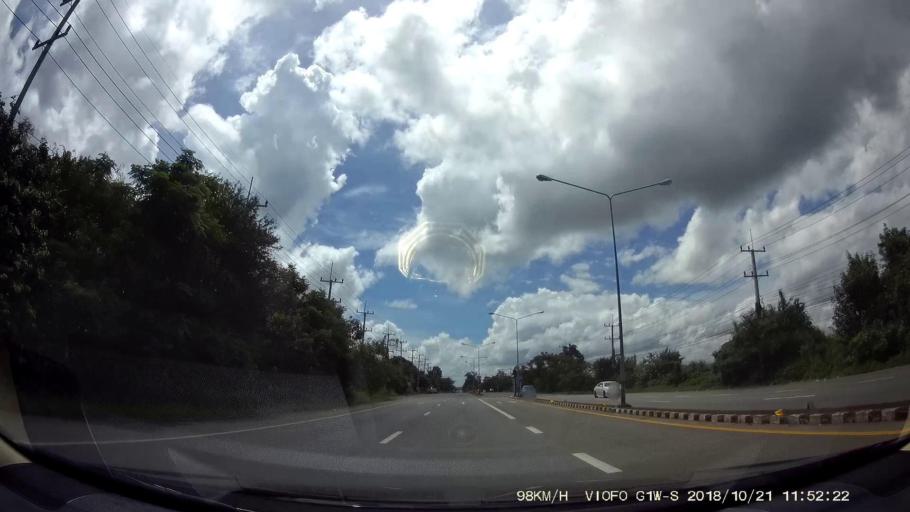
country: TH
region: Chaiyaphum
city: Chatturat
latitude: 15.6102
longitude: 101.9120
